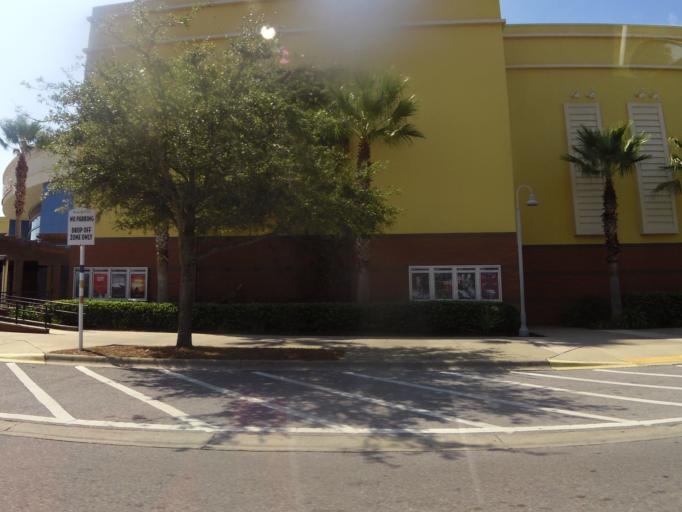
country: US
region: Florida
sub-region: Bay County
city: Laguna Beach
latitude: 30.2187
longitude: -85.8731
